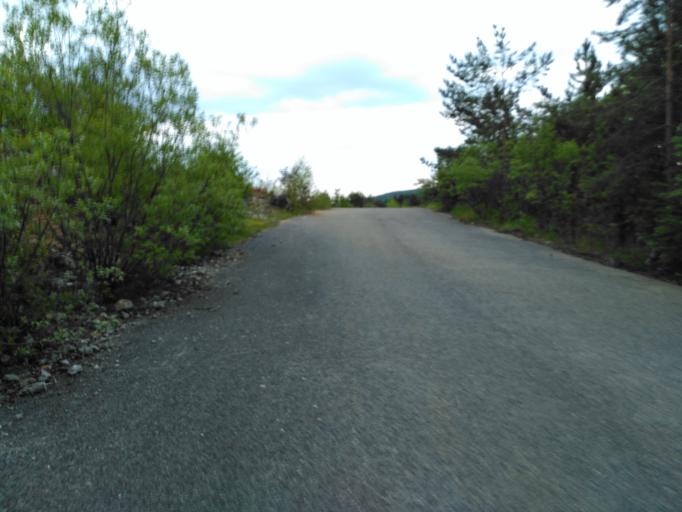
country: CZ
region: Central Bohemia
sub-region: Okres Beroun
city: Beroun
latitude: 49.9059
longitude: 14.0889
